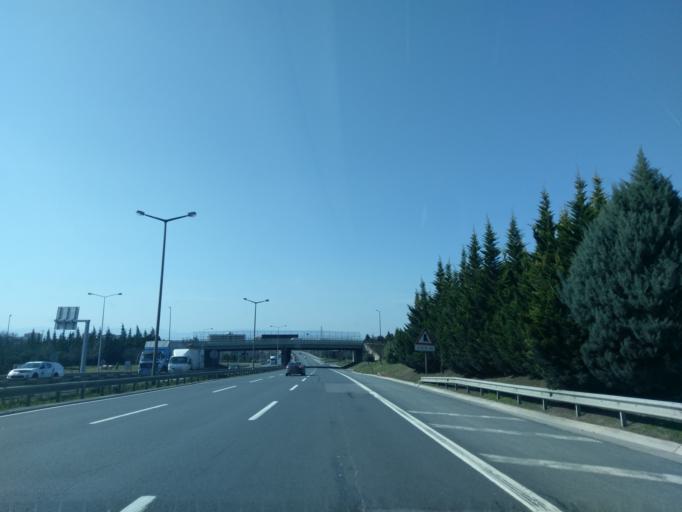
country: TR
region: Kocaeli
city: Balcik
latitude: 40.8645
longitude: 29.3849
